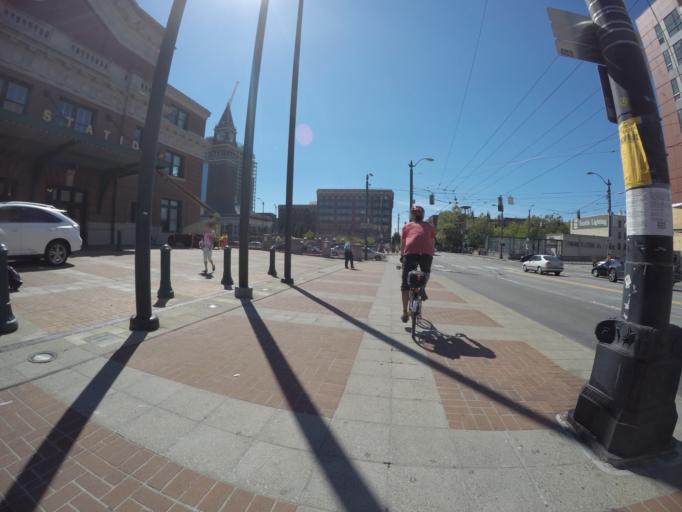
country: US
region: Washington
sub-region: King County
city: Seattle
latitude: 47.5991
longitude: -122.3284
